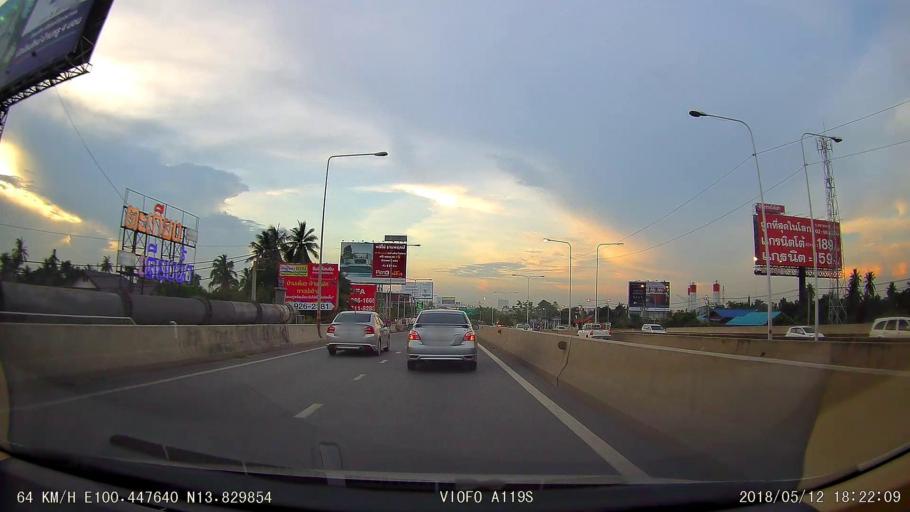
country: TH
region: Nonthaburi
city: Bang Kruai
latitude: 13.8300
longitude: 100.4476
